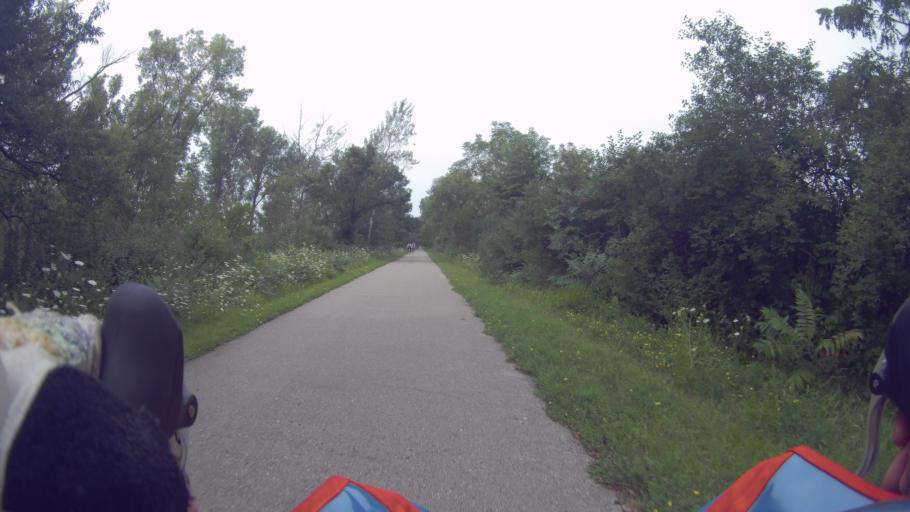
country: US
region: Wisconsin
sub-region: Dane County
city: Fitchburg
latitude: 43.0039
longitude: -89.4858
